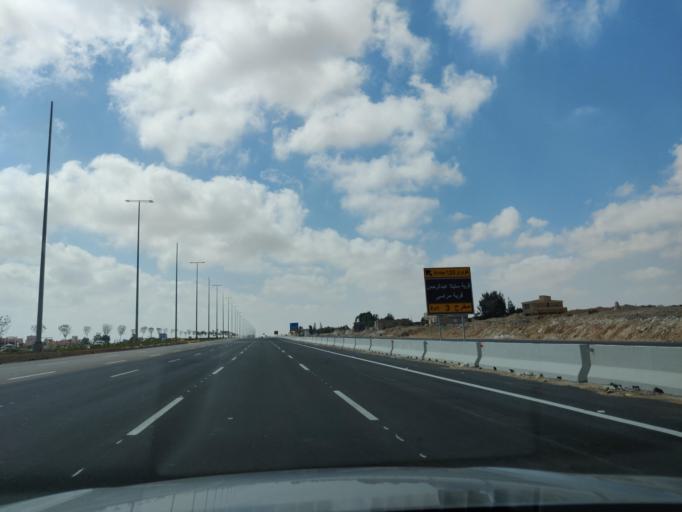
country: EG
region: Muhafazat Matruh
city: Al `Alamayn
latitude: 30.9336
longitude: 28.7892
